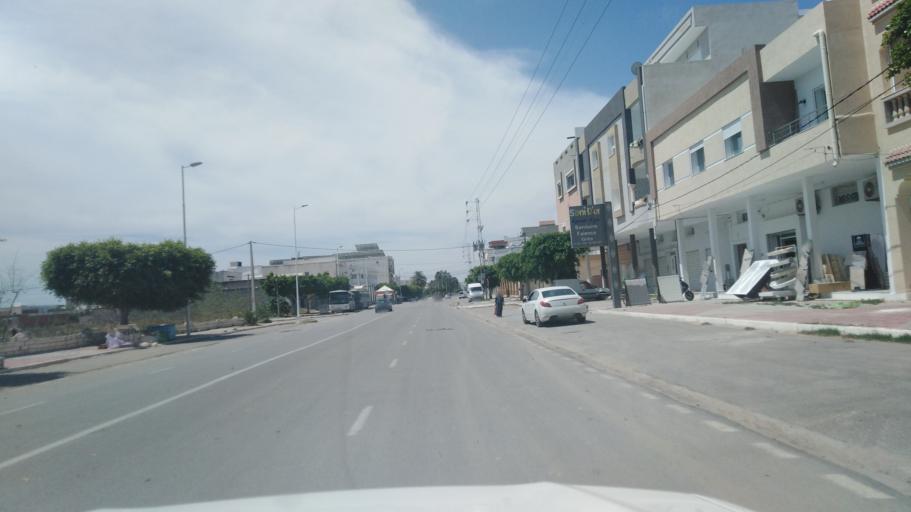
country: TN
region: Al Mahdiyah
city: Ksour Essaf
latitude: 35.4285
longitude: 11.0013
